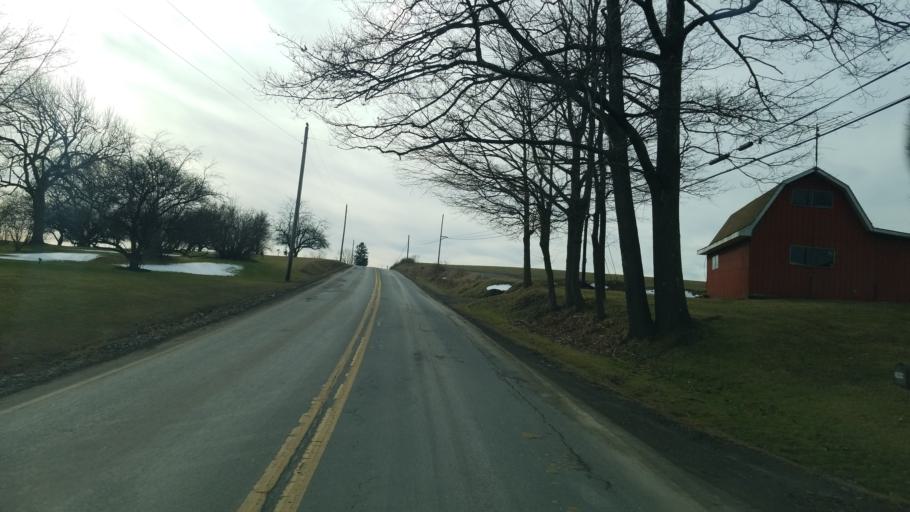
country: US
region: Pennsylvania
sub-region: Jefferson County
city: Punxsutawney
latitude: 40.8853
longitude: -79.0621
